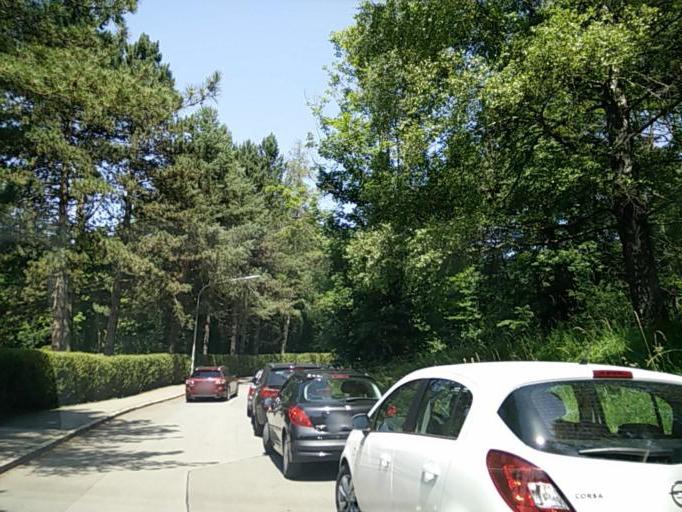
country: DE
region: Baden-Wuerttemberg
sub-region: Tuebingen Region
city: Gomaringen
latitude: 48.4115
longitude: 9.1314
